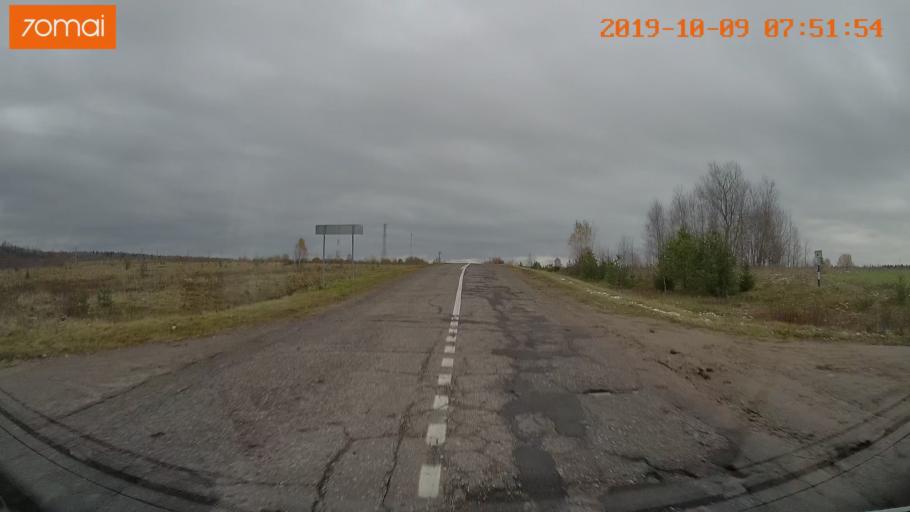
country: RU
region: Jaroslavl
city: Kukoboy
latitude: 58.6862
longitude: 39.8815
